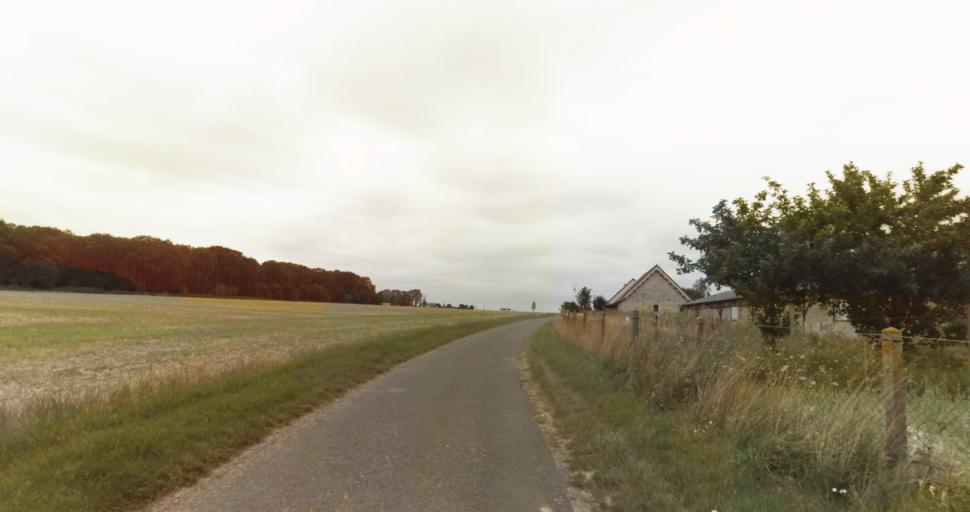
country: FR
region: Haute-Normandie
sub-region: Departement de l'Eure
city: Marcilly-sur-Eure
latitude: 48.9068
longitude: 1.3090
